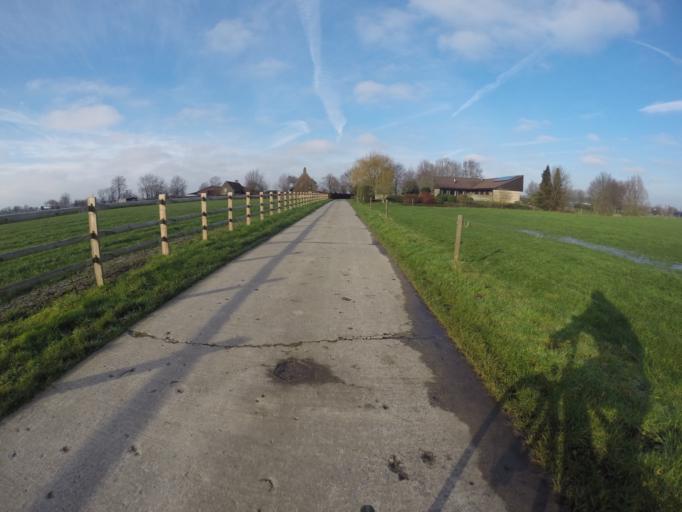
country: BE
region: Flanders
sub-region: Provincie Oost-Vlaanderen
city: Nevele
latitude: 51.0457
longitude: 3.5153
